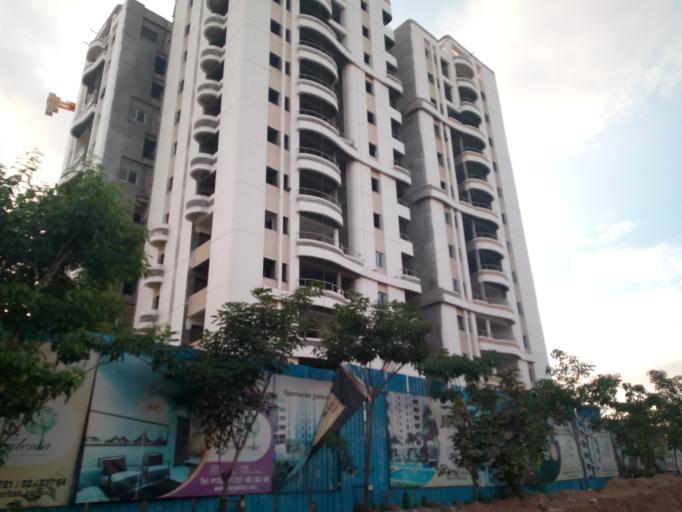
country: IN
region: Telangana
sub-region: Rangareddi
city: Kukatpalli
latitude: 17.4346
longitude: 78.3744
